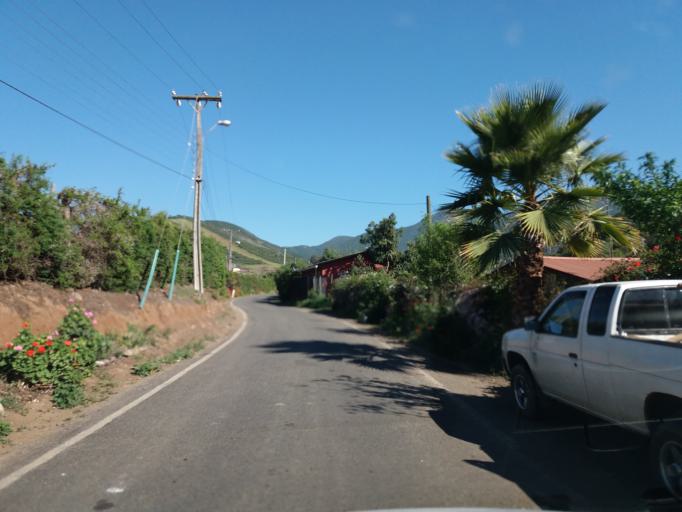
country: CL
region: Valparaiso
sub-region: Provincia de Quillota
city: Quillota
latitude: -32.8617
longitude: -71.2808
